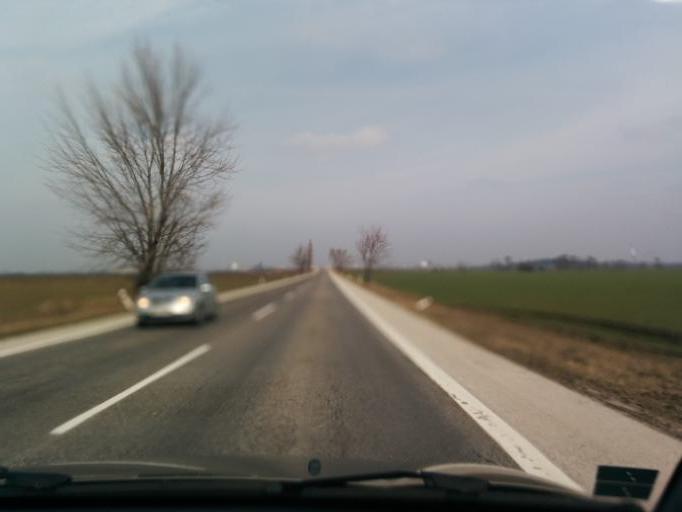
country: SK
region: Trnavsky
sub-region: Okres Galanta
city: Galanta
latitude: 48.2514
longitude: 17.7077
